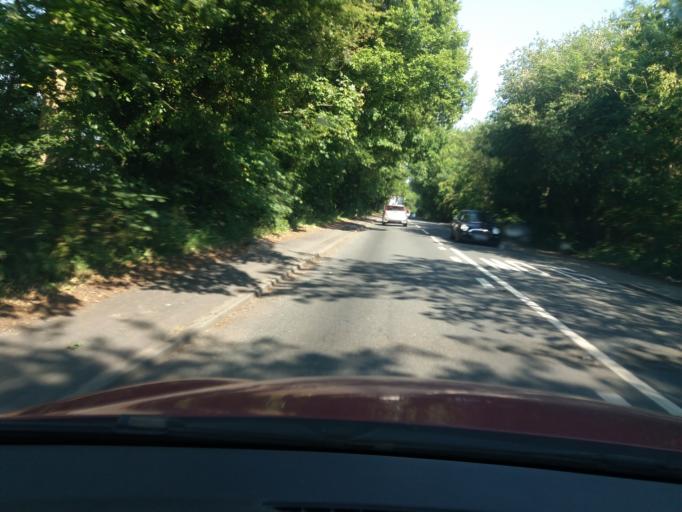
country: GB
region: England
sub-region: Lancashire
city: Clayton-le-Woods
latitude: 53.6845
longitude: -2.6552
